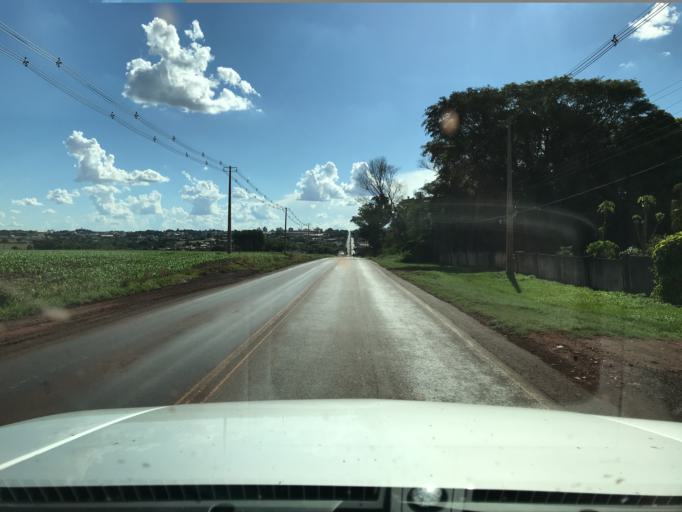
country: BR
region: Parana
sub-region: Palotina
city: Palotina
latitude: -24.2762
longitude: -53.8143
